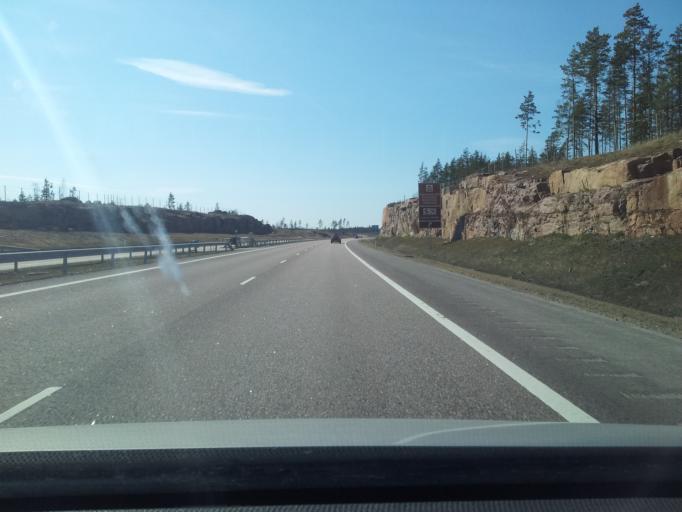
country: FI
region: Kymenlaakso
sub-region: Kotka-Hamina
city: Pyhtaeae
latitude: 60.4896
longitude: 26.5816
